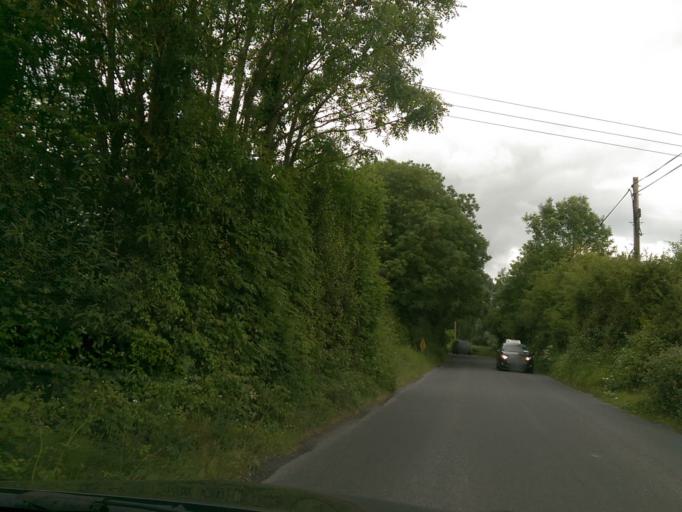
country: IE
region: Munster
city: Thurles
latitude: 52.6673
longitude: -7.7973
